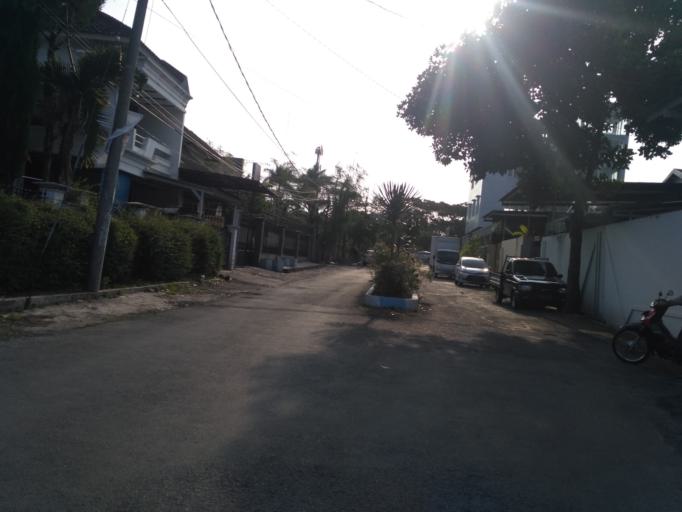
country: ID
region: East Java
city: Malang
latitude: -7.9388
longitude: 112.6265
